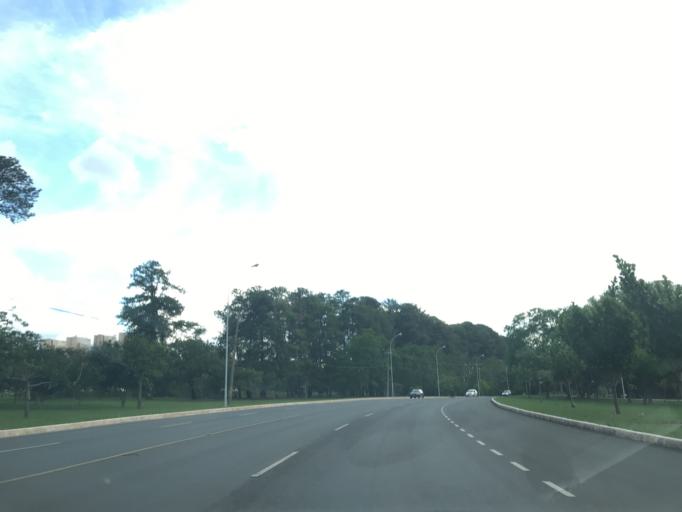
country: BR
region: Federal District
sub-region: Brasilia
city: Brasilia
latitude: -15.8070
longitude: -47.9262
